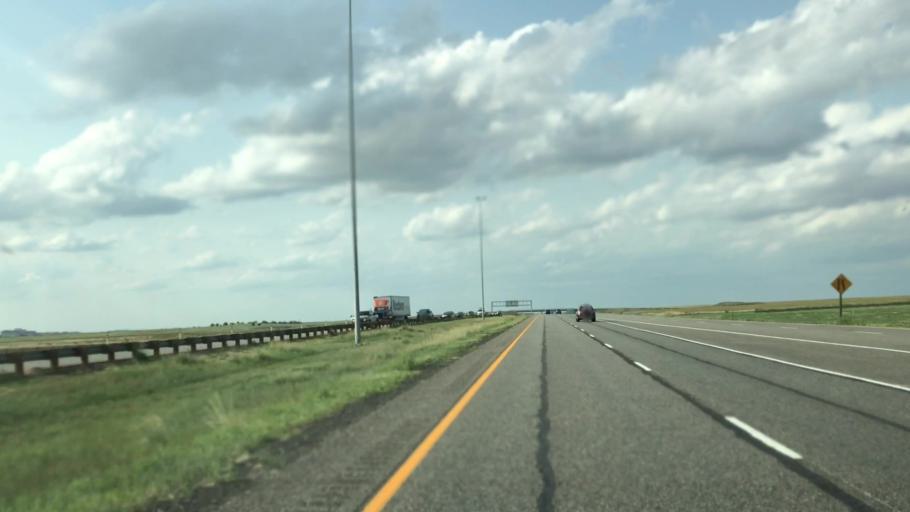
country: US
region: Colorado
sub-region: Adams County
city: Aurora
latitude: 39.7729
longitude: -104.7164
